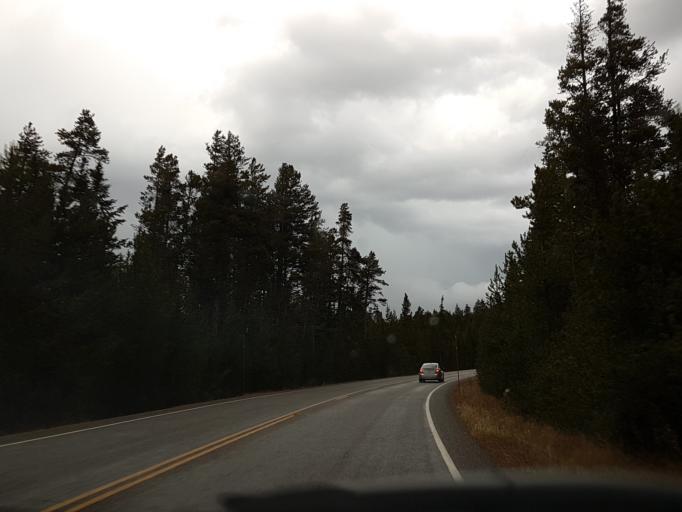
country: US
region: Montana
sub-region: Gallatin County
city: West Yellowstone
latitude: 44.4554
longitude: -110.5076
